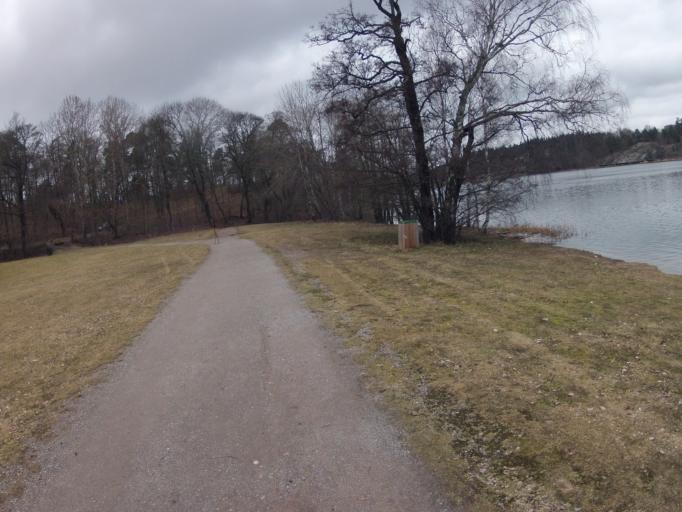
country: SE
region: Stockholm
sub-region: Norrtalje Kommun
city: Bergshamra
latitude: 59.3745
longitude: 18.0217
